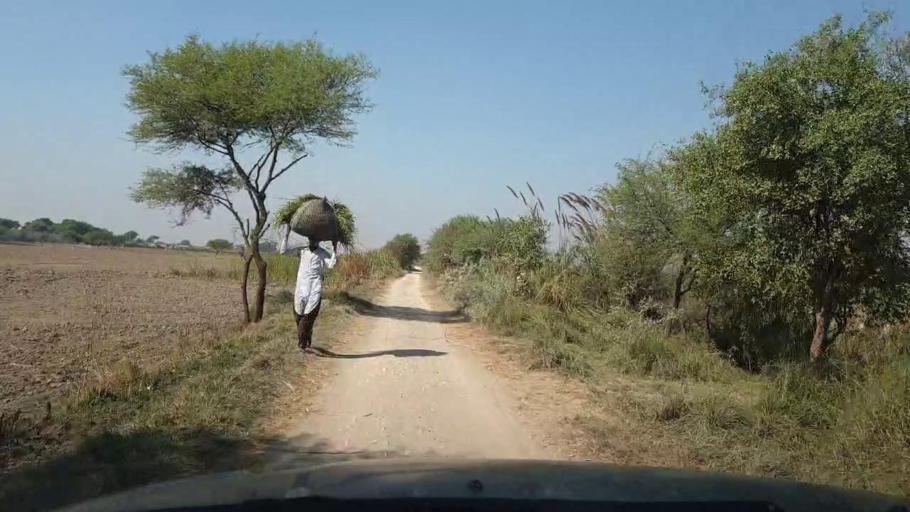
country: PK
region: Sindh
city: Tando Muhammad Khan
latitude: 24.9882
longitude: 68.5058
